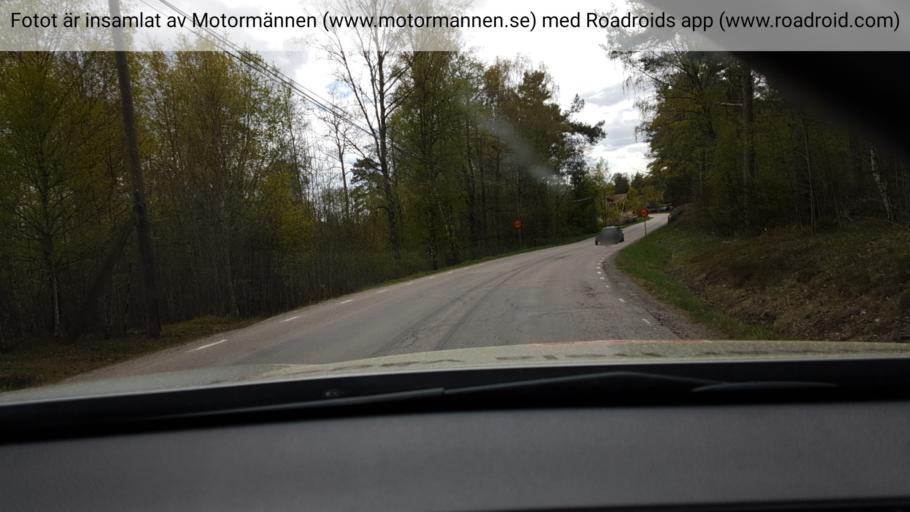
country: SE
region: Stockholm
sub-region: Haninge Kommun
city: Haninge
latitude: 59.0913
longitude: 18.1805
